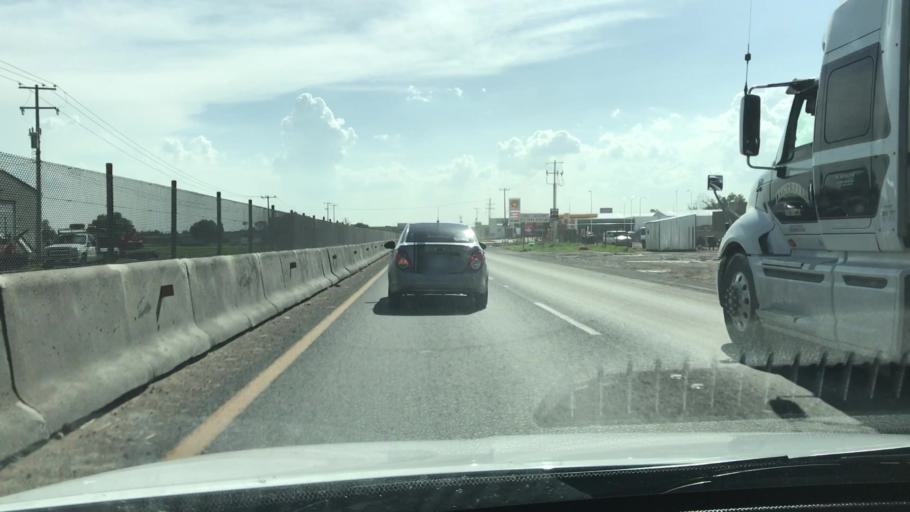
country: MX
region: Guanajuato
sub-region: Celaya
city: Colonia Pedro Maria Anaya
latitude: 20.5177
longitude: -100.8640
